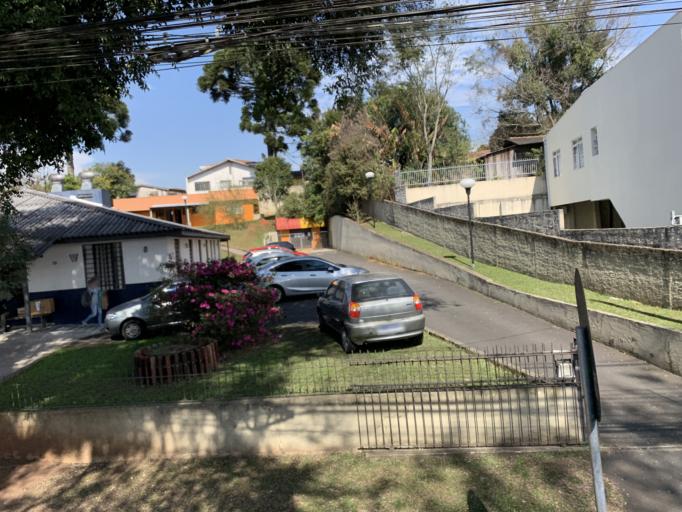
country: BR
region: Parana
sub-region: Curitiba
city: Curitiba
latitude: -25.4020
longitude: -49.3286
